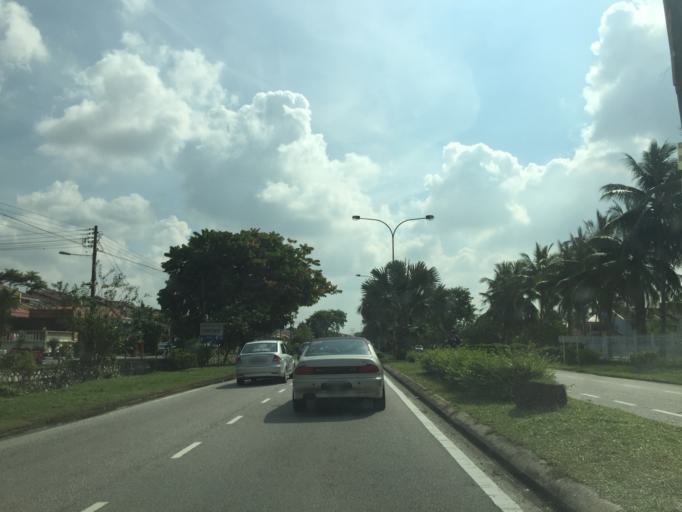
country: MY
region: Selangor
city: Klang
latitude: 3.0155
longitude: 101.4505
